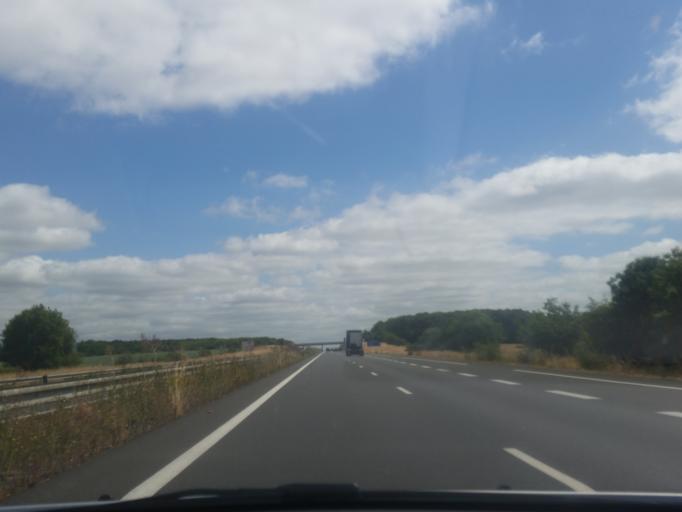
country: FR
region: Pays de la Loire
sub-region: Departement de Maine-et-Loire
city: Saint-Georges-sur-Loire
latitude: 47.4352
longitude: -0.7844
